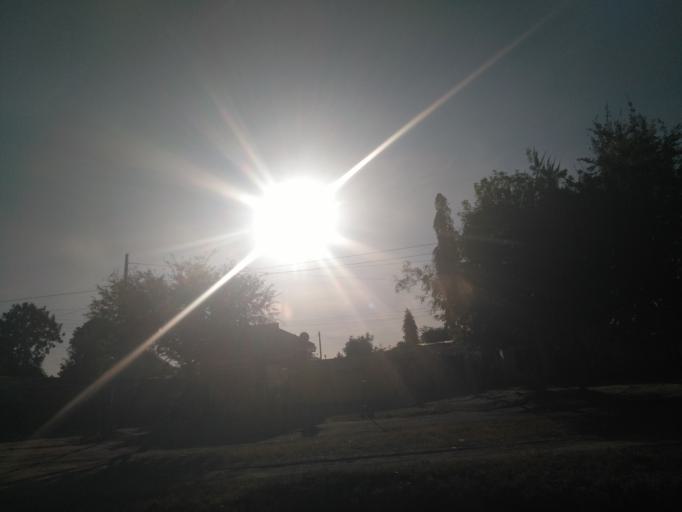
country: TZ
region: Dodoma
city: Dodoma
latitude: -6.1574
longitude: 35.7466
